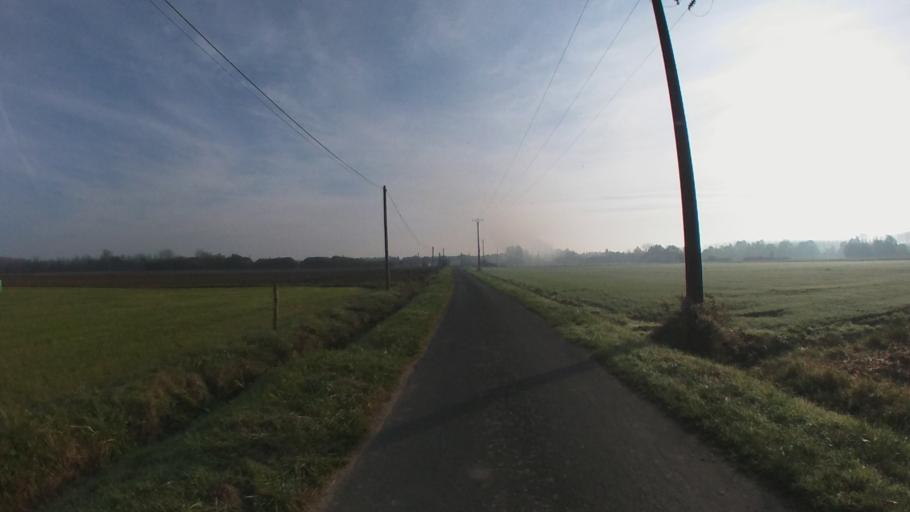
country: FR
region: Pays de la Loire
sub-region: Departement de la Sarthe
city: La Fleche
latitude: 47.7065
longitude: -0.1228
